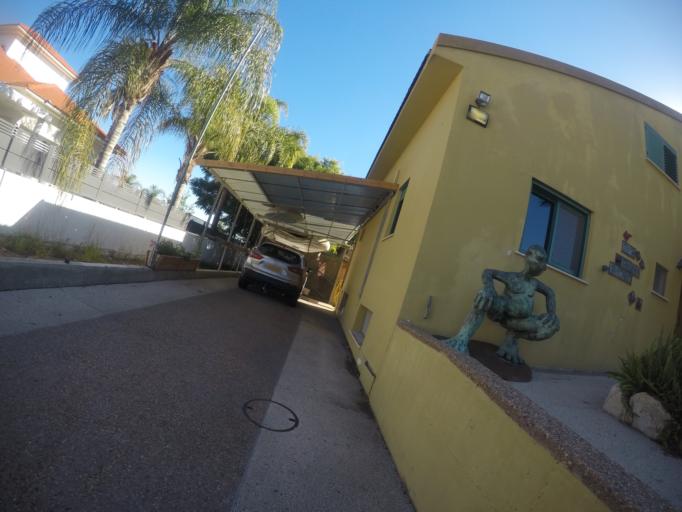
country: IL
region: Southern District
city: Qiryat Gat
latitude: 31.6224
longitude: 34.7095
